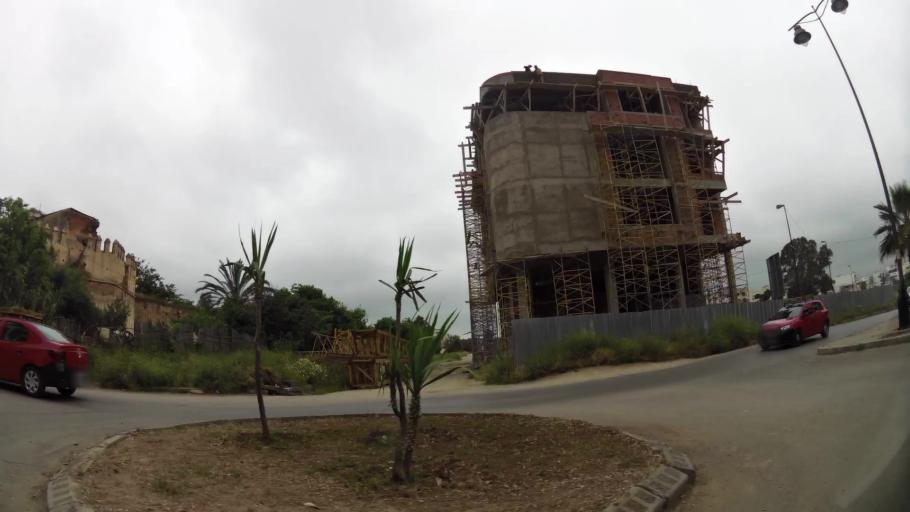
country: MA
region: Fes-Boulemane
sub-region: Fes
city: Fes
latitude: 34.0265
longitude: -5.0005
